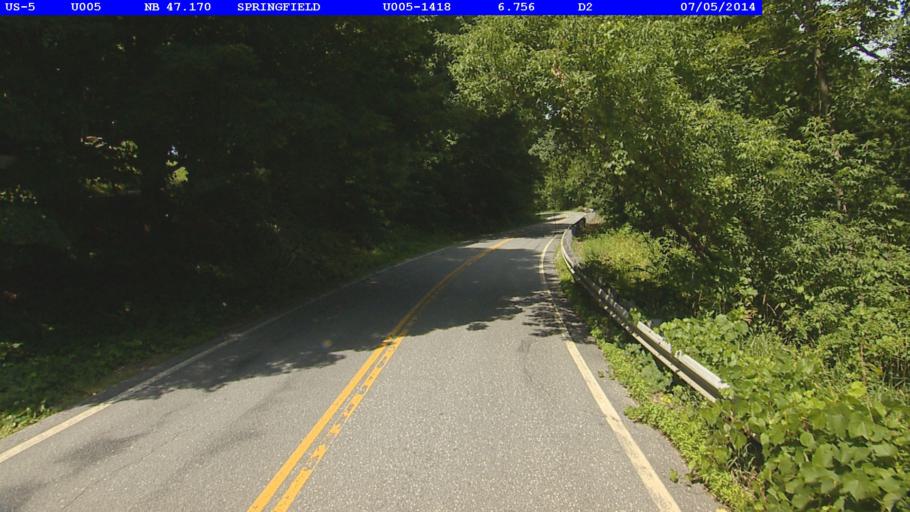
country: US
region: New Hampshire
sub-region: Sullivan County
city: Charlestown
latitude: 43.3081
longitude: -72.3998
